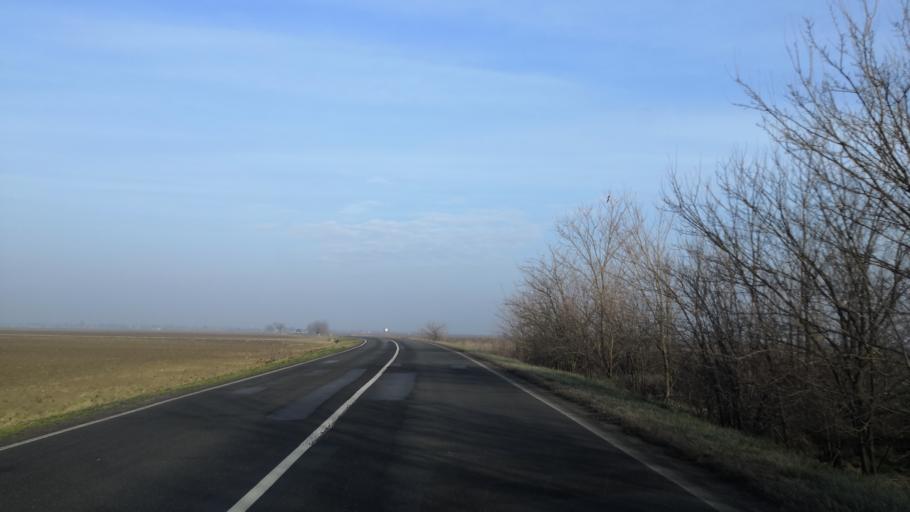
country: RS
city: Rumenka
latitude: 45.3238
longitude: 19.7374
